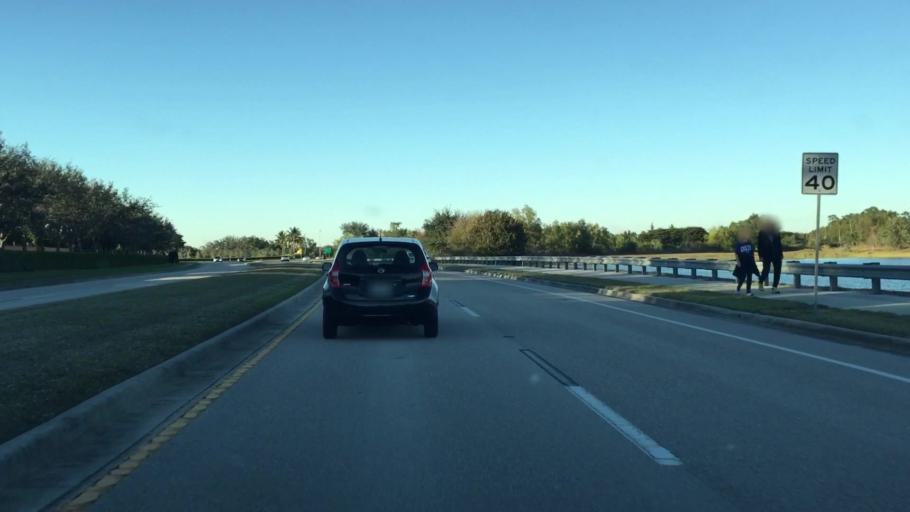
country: US
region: Florida
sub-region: Lee County
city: Estero
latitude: 26.4154
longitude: -81.8062
